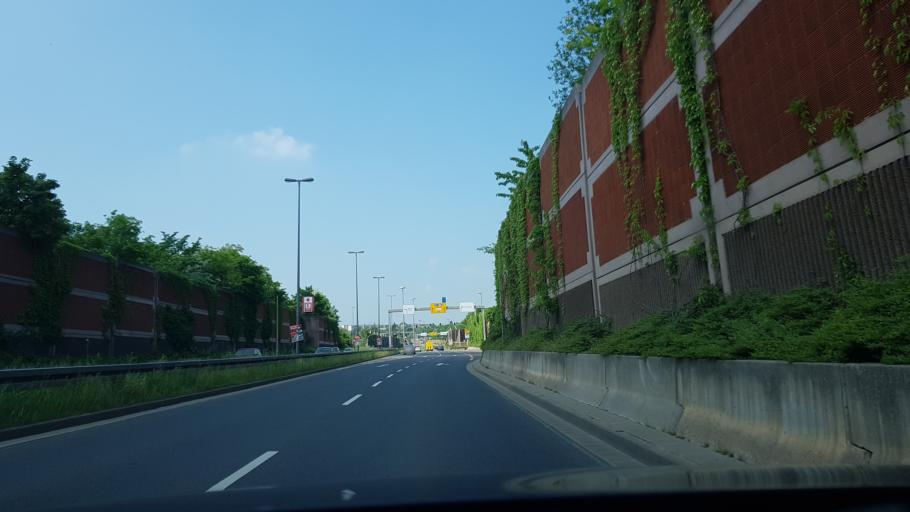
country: DE
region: Saxony
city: Dresden
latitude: 51.0481
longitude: 13.6840
